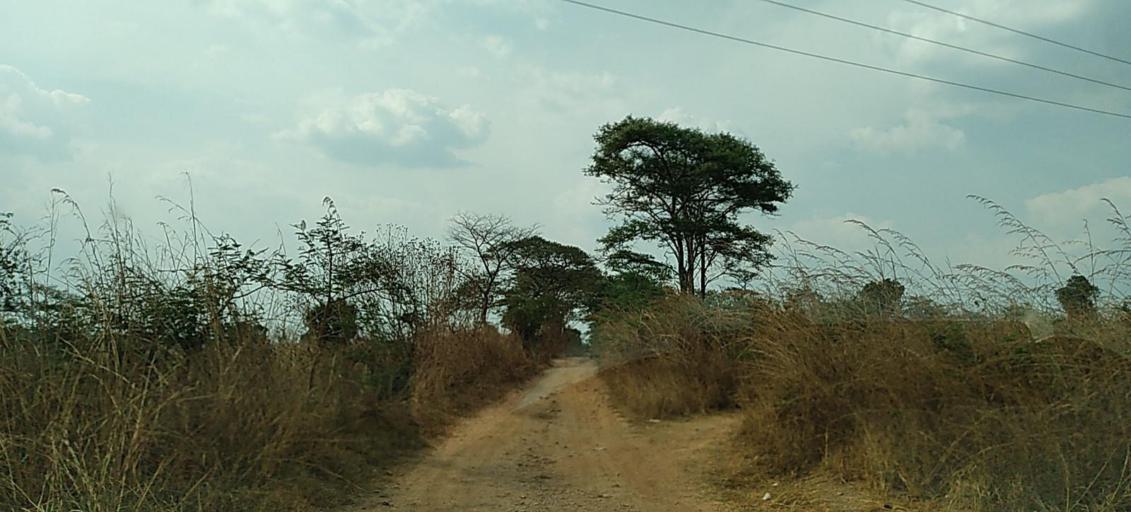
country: ZM
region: Copperbelt
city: Chililabombwe
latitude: -12.3966
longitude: 27.8042
